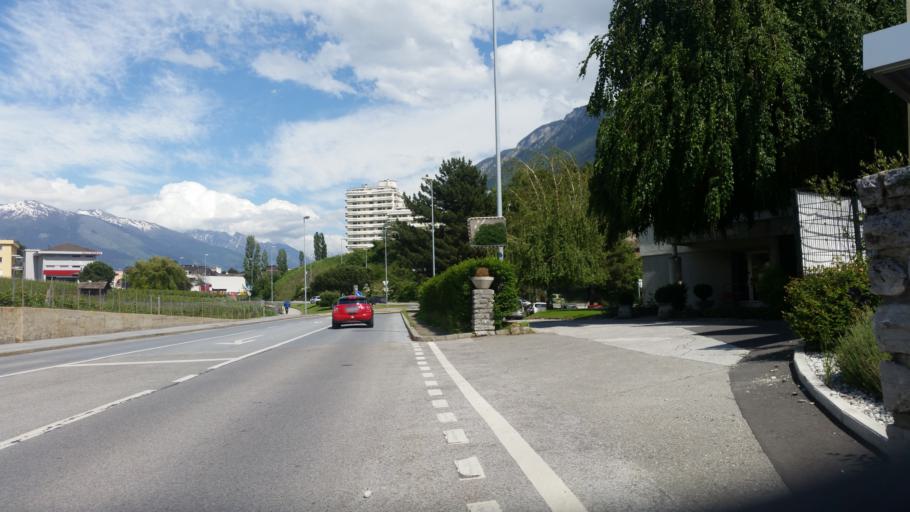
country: CH
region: Valais
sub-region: Sierre District
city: Chalais
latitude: 46.2834
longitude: 7.5125
